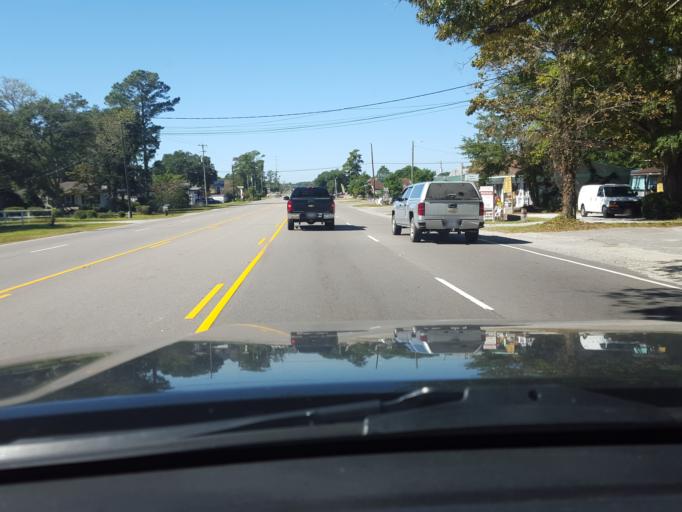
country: US
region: North Carolina
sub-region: New Hanover County
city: Seagate
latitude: 34.2093
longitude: -77.8453
